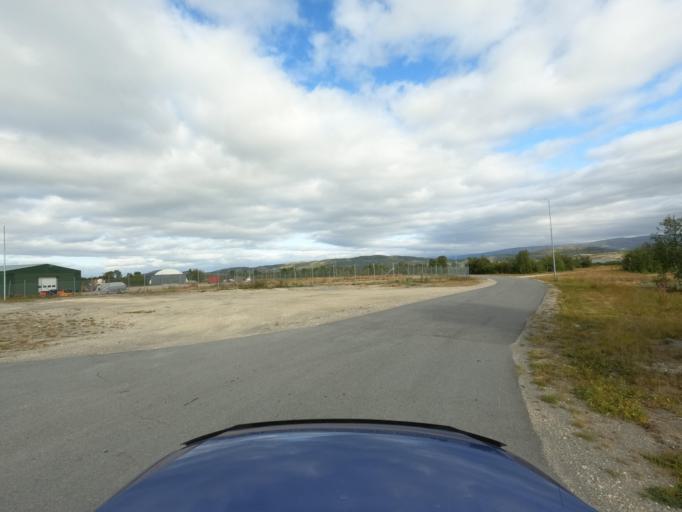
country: NO
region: Finnmark Fylke
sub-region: Porsanger
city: Lakselv
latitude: 70.0660
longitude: 24.9847
